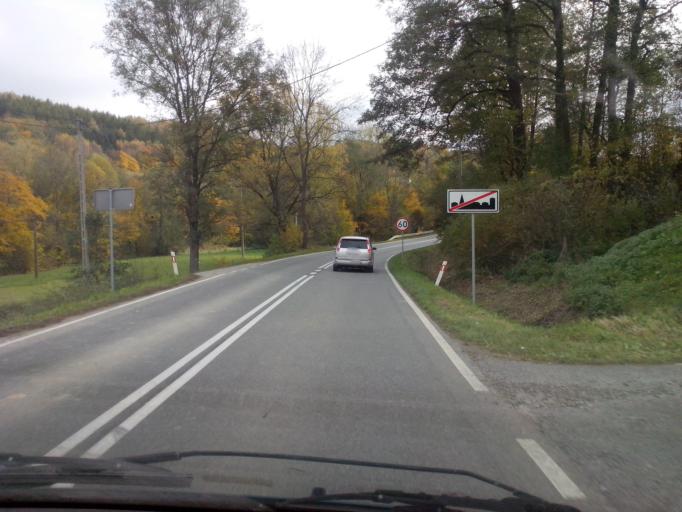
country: PL
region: Subcarpathian Voivodeship
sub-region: Powiat strzyzowski
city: Wisniowa
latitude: 49.8861
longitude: 21.6468
